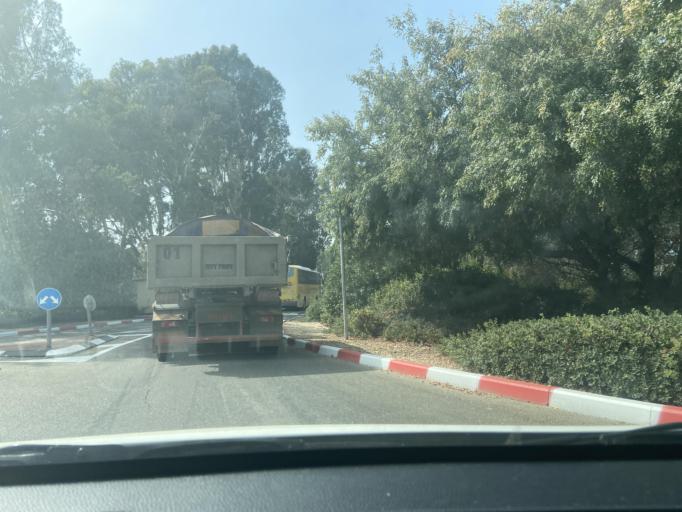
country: IL
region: Northern District
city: Nahariya
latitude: 33.0446
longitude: 35.1087
